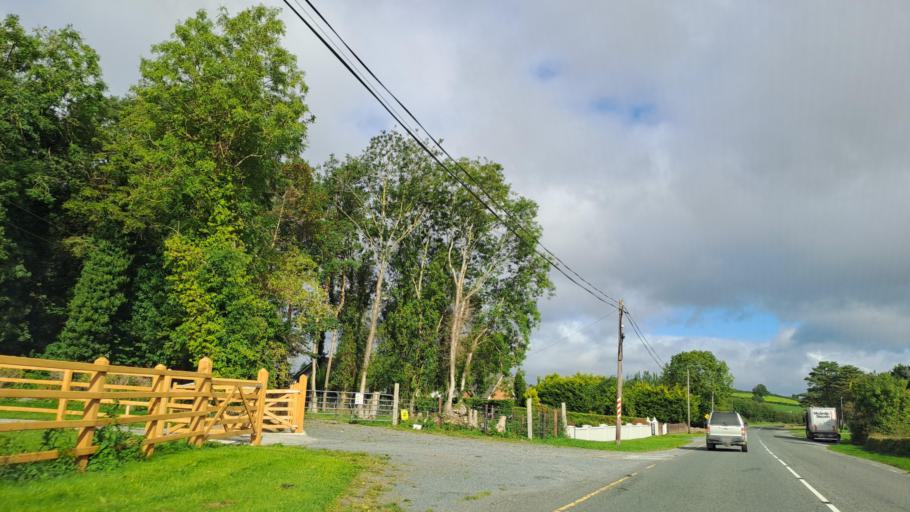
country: IE
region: Ulster
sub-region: County Monaghan
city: Carrickmacross
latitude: 53.9509
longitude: -6.7594
